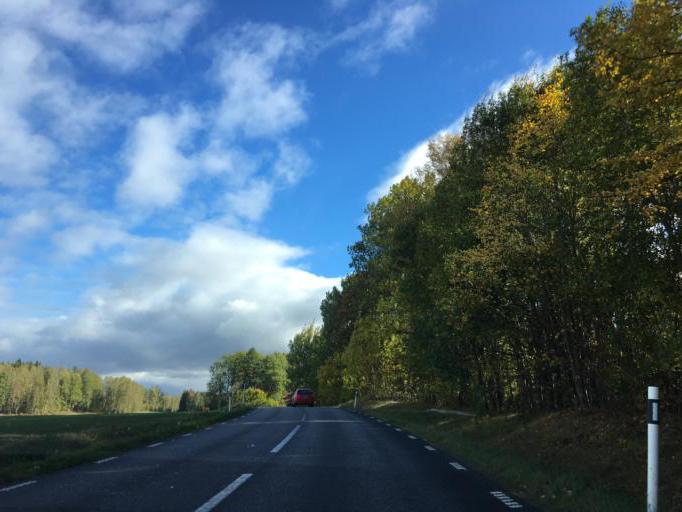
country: SE
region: Soedermanland
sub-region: Nykopings Kommun
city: Olstorp
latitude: 58.9077
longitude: 16.5435
